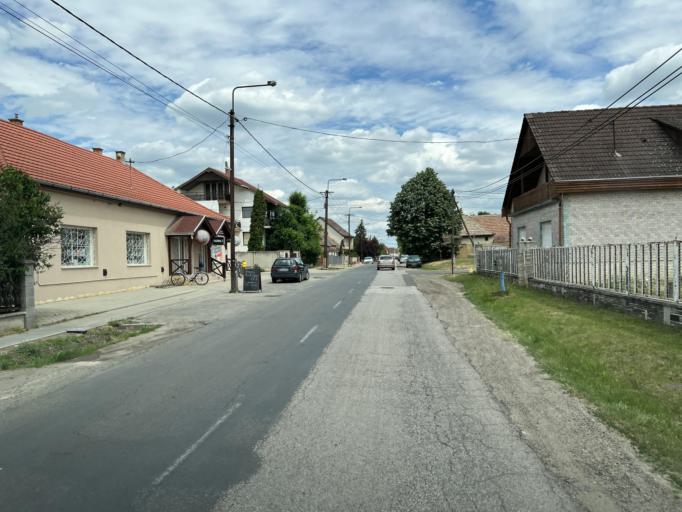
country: HU
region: Pest
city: Toalmas
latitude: 47.5080
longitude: 19.6632
